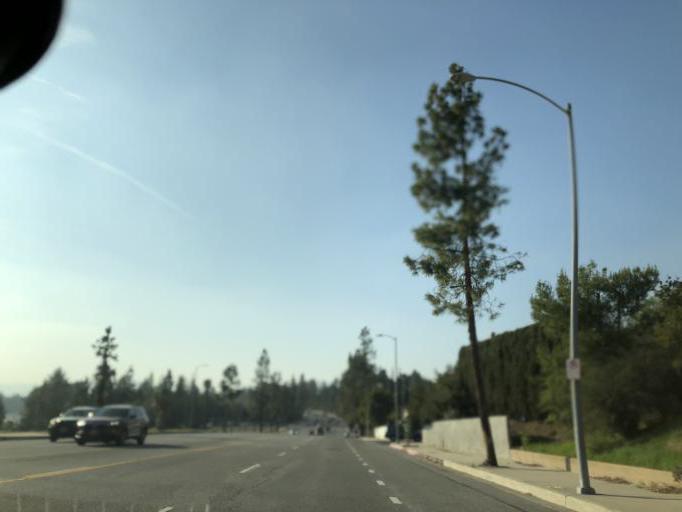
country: US
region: California
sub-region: Los Angeles County
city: Northridge
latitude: 34.2752
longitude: -118.5443
